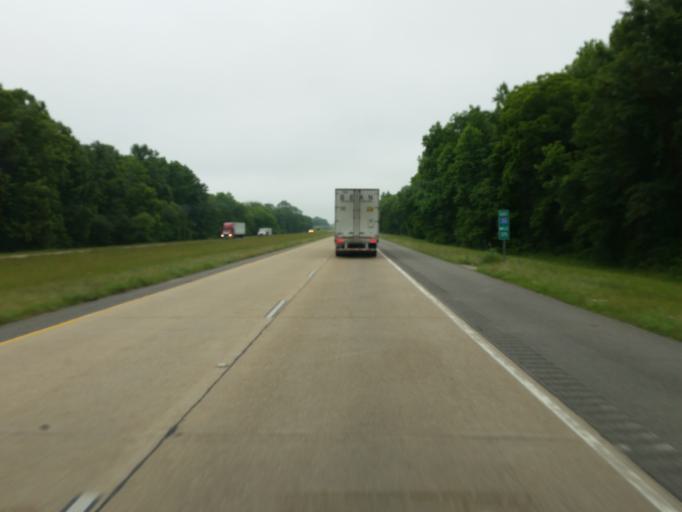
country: US
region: Louisiana
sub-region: Madison Parish
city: Tallulah
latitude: 32.3705
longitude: -91.1410
